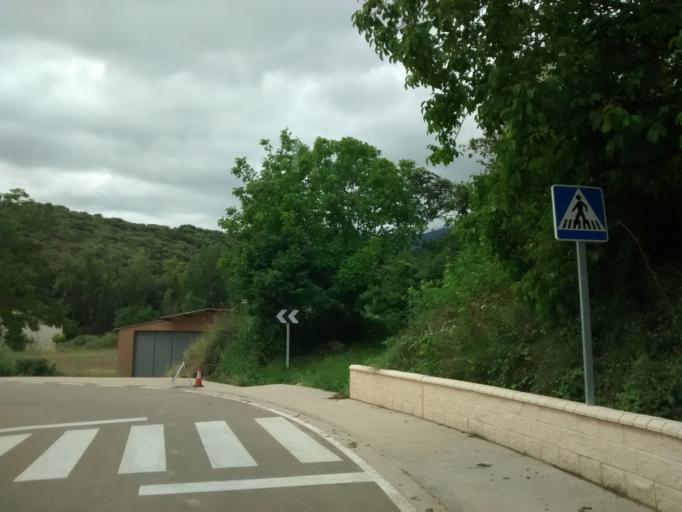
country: ES
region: Aragon
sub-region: Provincia de Zaragoza
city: Lituenigo
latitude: 41.8335
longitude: -1.7629
